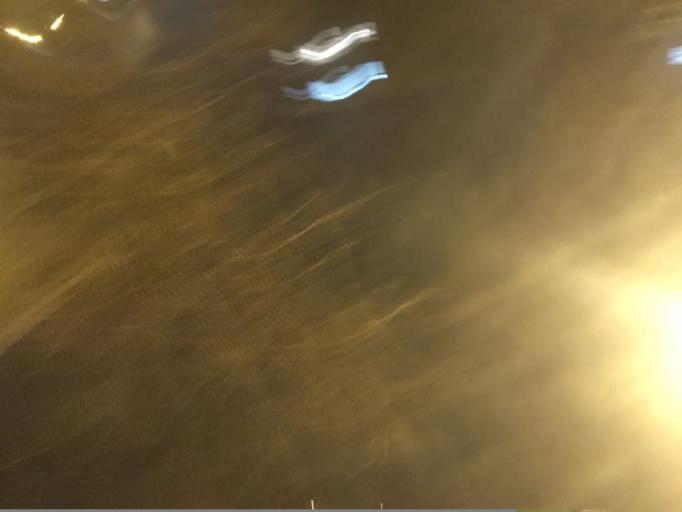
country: TR
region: Istanbul
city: Maltepe
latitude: 40.9247
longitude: 29.1445
